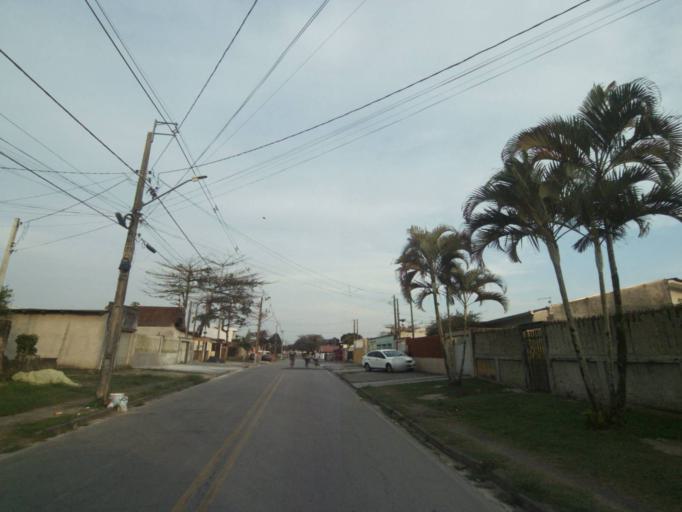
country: BR
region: Parana
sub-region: Paranagua
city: Paranagua
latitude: -25.5222
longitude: -48.5364
